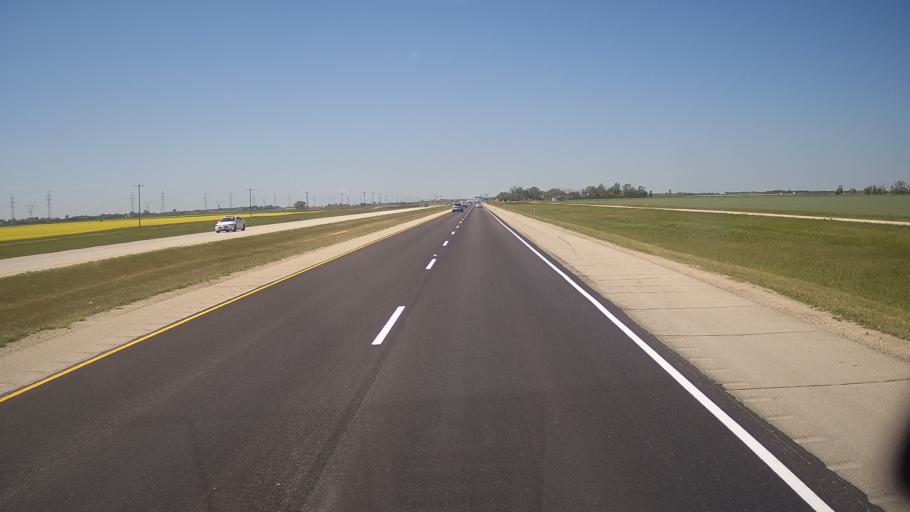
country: CA
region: Manitoba
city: Winnipeg
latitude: 49.9906
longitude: -97.1954
